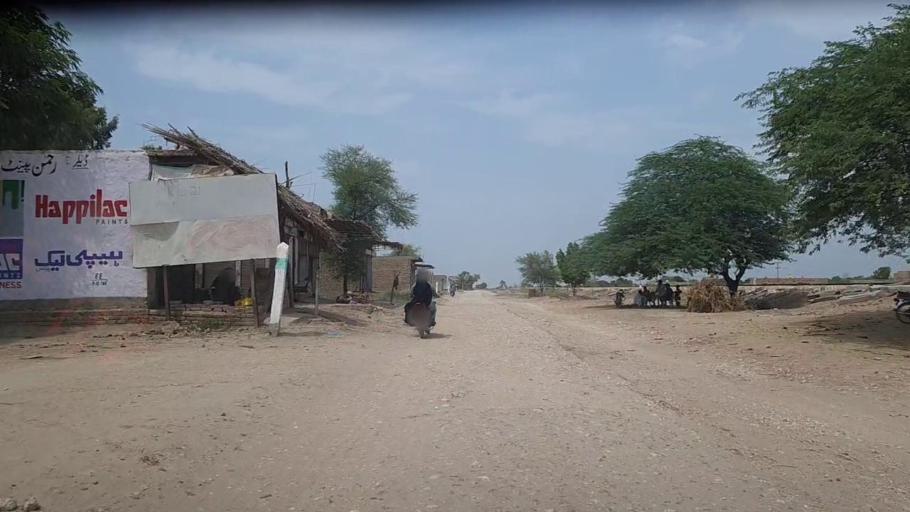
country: PK
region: Sindh
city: Bhiria
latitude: 26.8993
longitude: 68.2880
